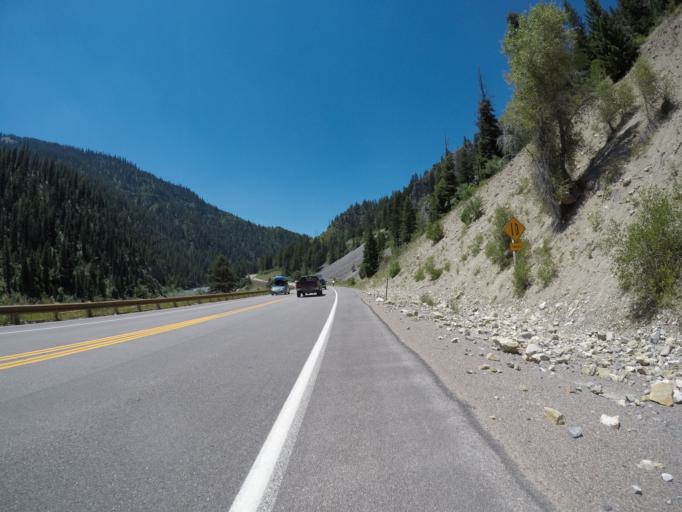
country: US
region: Wyoming
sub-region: Teton County
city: Hoback
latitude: 43.1983
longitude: -110.9061
